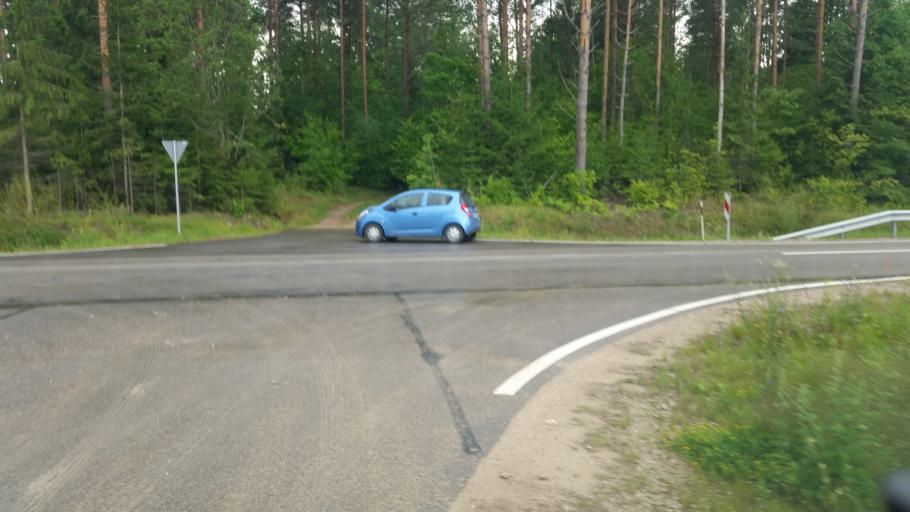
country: LV
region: Vecumnieki
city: Vecumnieki
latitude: 56.4381
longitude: 24.6106
